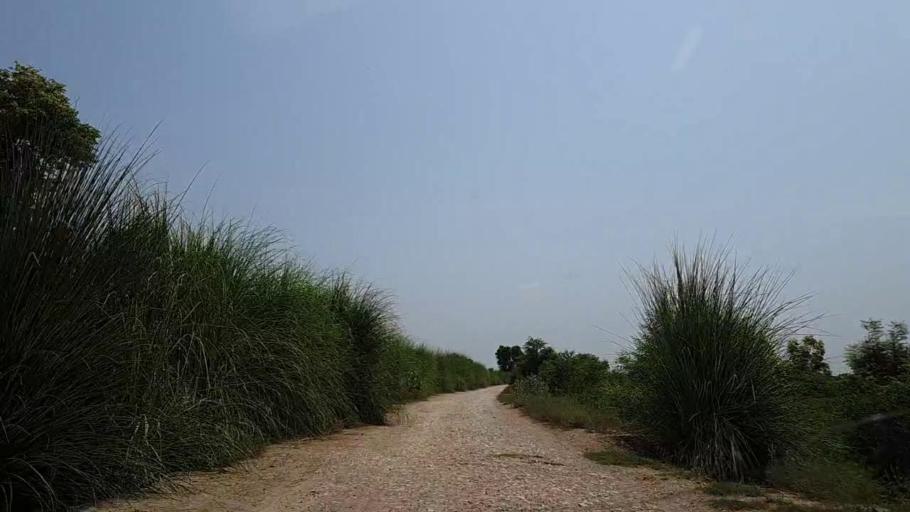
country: PK
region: Sindh
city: Adilpur
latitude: 27.9394
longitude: 69.3959
